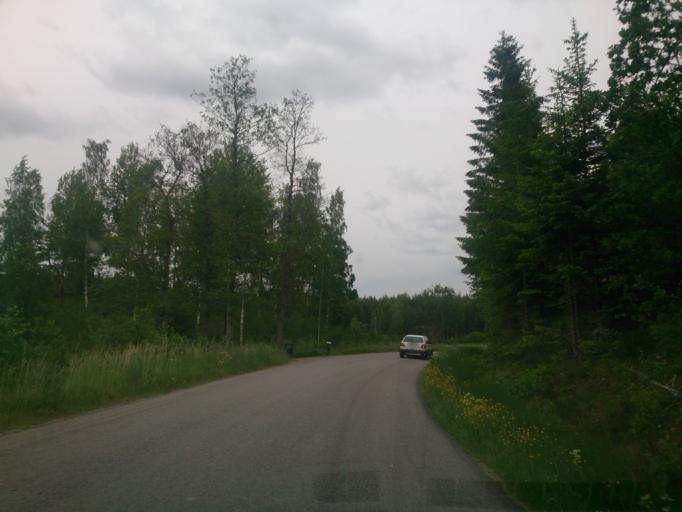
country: SE
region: OEstergoetland
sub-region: Valdemarsviks Kommun
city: Gusum
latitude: 58.3181
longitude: 16.3753
